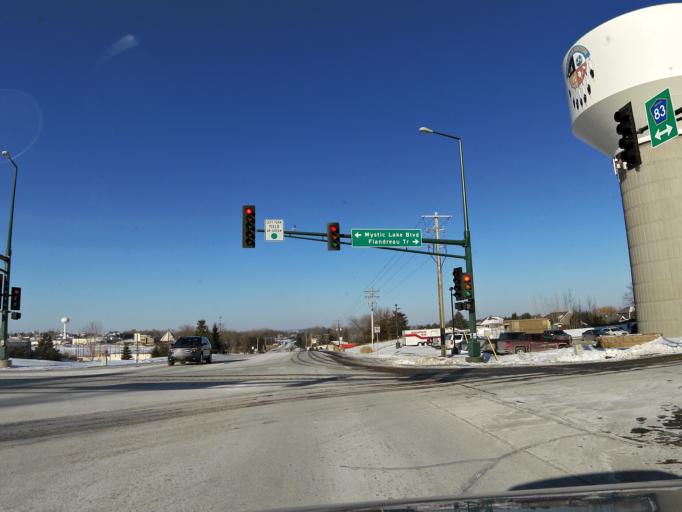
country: US
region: Minnesota
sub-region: Scott County
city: Prior Lake
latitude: 44.7290
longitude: -93.4695
